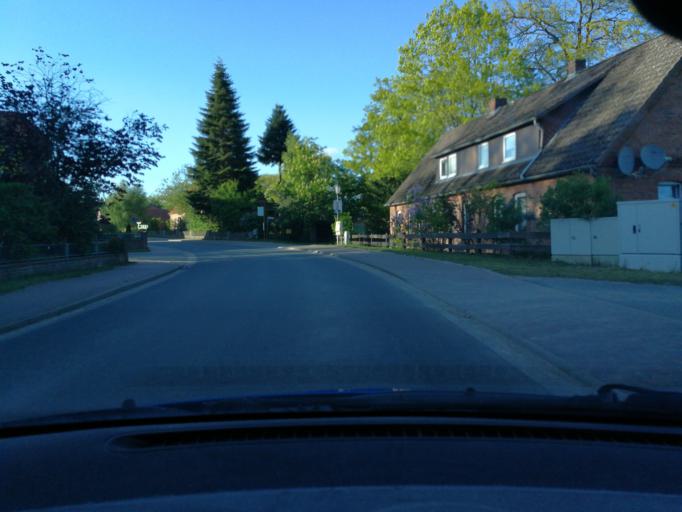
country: DE
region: Lower Saxony
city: Betzendorf
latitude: 53.1110
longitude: 10.3024
